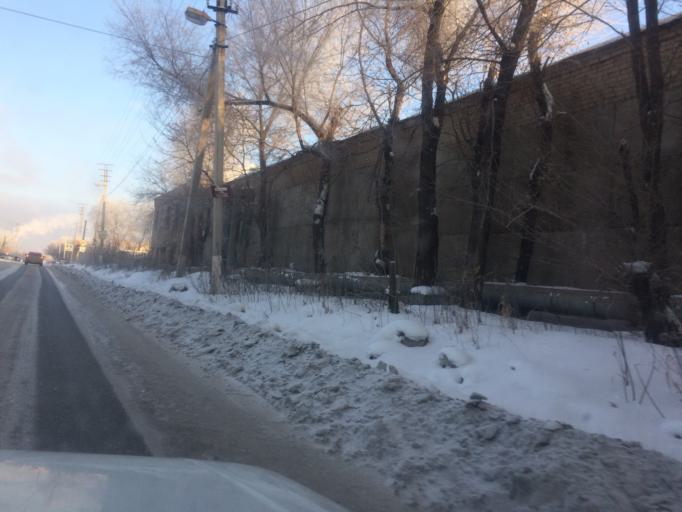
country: RU
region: Chelyabinsk
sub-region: Gorod Magnitogorsk
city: Magnitogorsk
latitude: 53.3941
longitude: 59.0708
